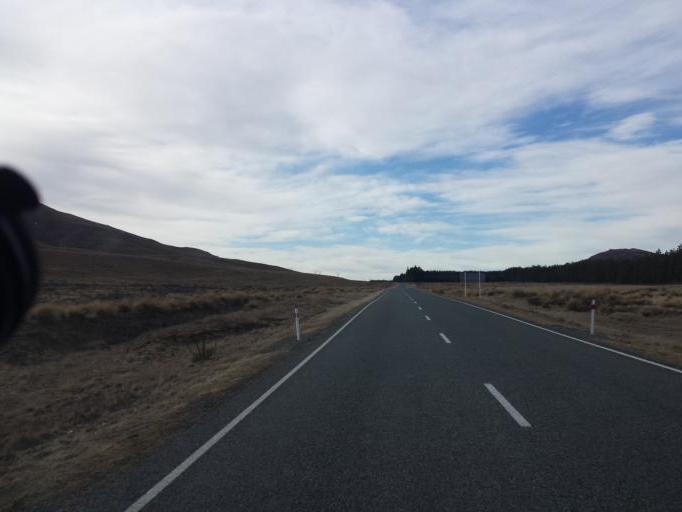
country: NZ
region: Canterbury
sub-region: Timaru District
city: Pleasant Point
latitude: -44.0927
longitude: 170.5754
